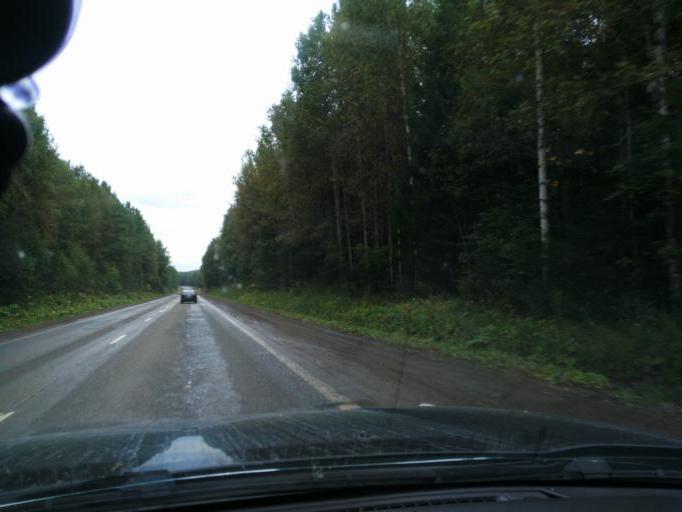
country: RU
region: Perm
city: Chernushka
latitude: 56.6954
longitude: 56.1820
